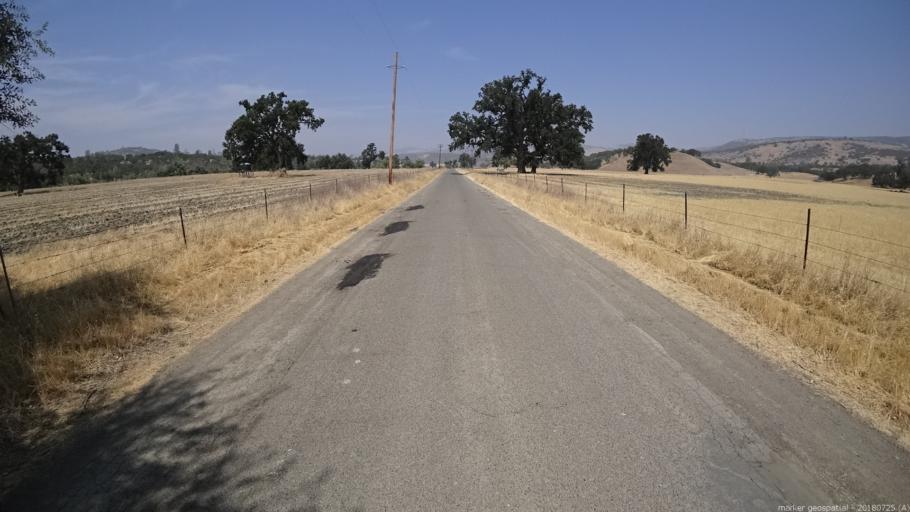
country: US
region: California
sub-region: Fresno County
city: Coalinga
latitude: 35.9037
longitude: -120.4335
